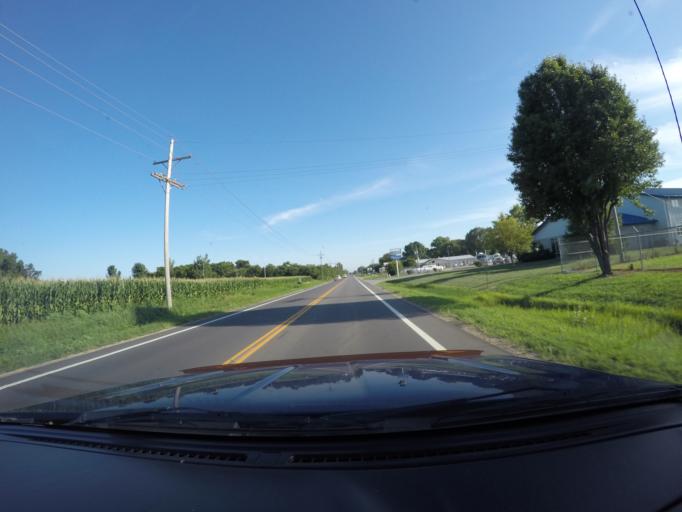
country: US
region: Kansas
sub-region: Douglas County
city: Lawrence
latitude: 39.0090
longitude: -95.2337
